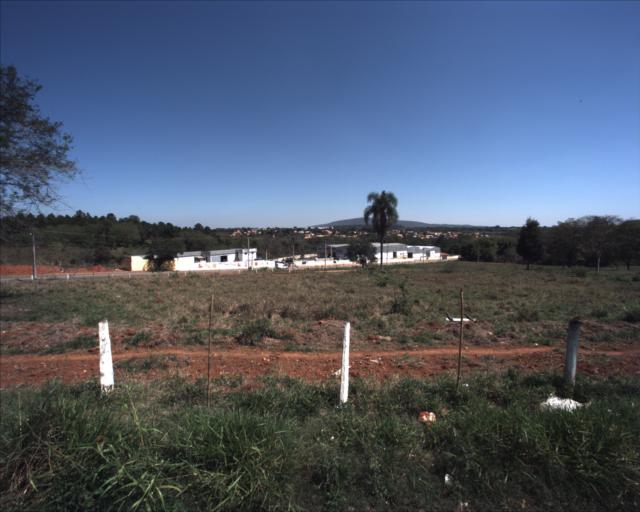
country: BR
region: Sao Paulo
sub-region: Aracoiaba Da Serra
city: Aracoiaba da Serra
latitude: -23.4409
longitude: -47.5393
